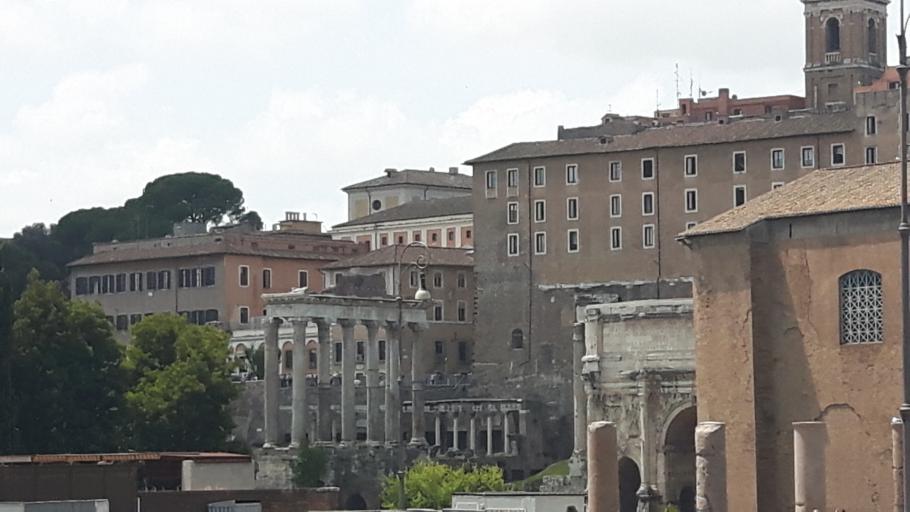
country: IT
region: Latium
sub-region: Citta metropolitana di Roma Capitale
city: Rome
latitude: 41.8932
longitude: 12.4868
